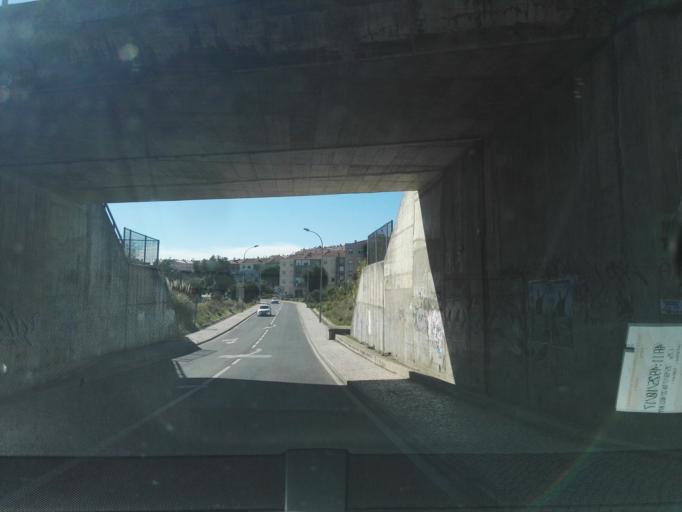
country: PT
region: Lisbon
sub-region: Sintra
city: Rio de Mouro
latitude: 38.7904
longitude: -9.3274
